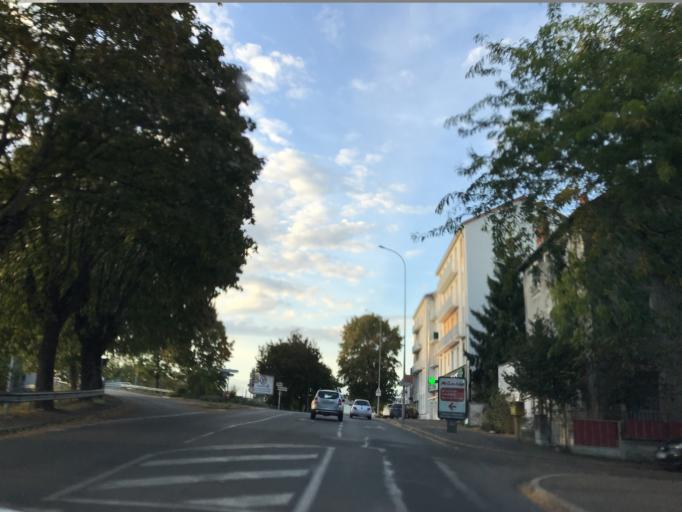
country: FR
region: Auvergne
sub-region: Departement de l'Allier
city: Vichy
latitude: 46.1178
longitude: 3.4364
